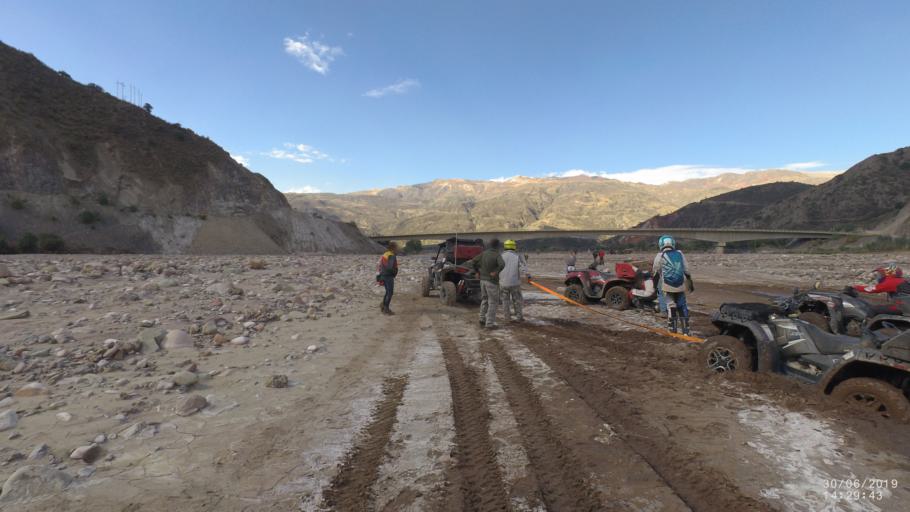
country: BO
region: Cochabamba
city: Irpa Irpa
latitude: -17.7998
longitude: -66.3526
